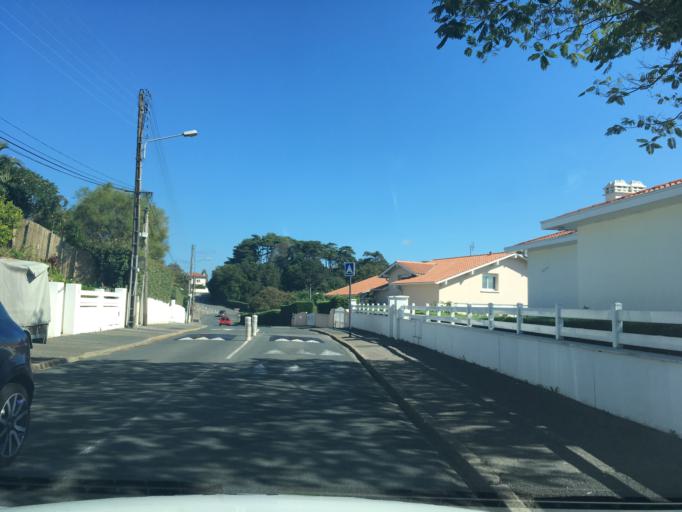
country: FR
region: Aquitaine
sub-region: Departement des Pyrenees-Atlantiques
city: Biarritz
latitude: 43.4636
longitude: -1.5646
